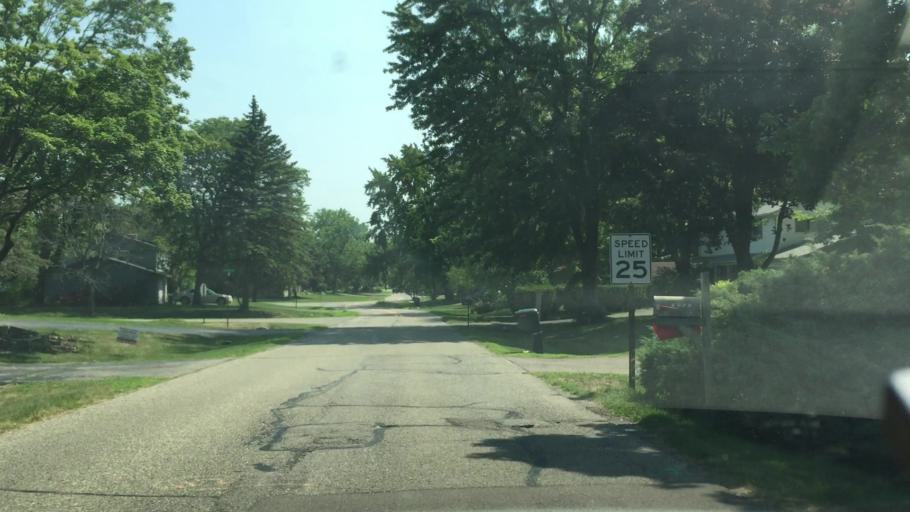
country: US
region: Michigan
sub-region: Oakland County
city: West Bloomfield Township
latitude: 42.5325
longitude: -83.3549
